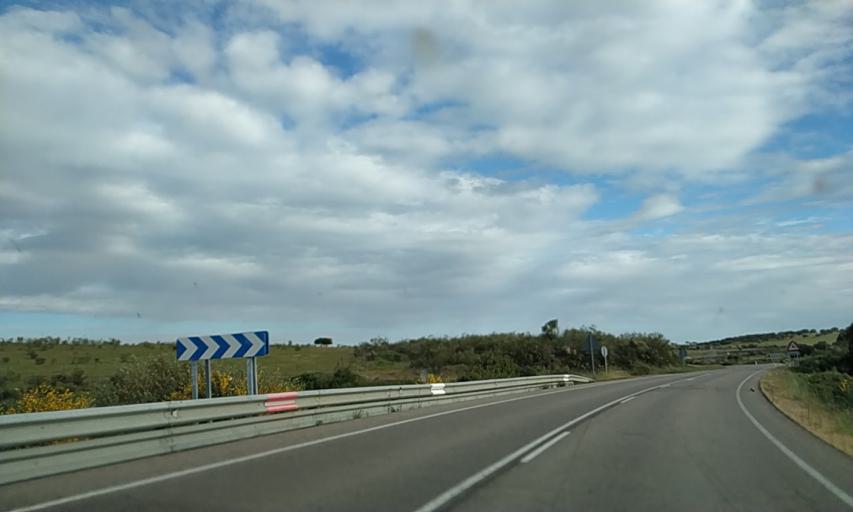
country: ES
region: Extremadura
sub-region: Provincia de Caceres
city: Perales del Puerto
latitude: 40.1221
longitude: -6.6734
